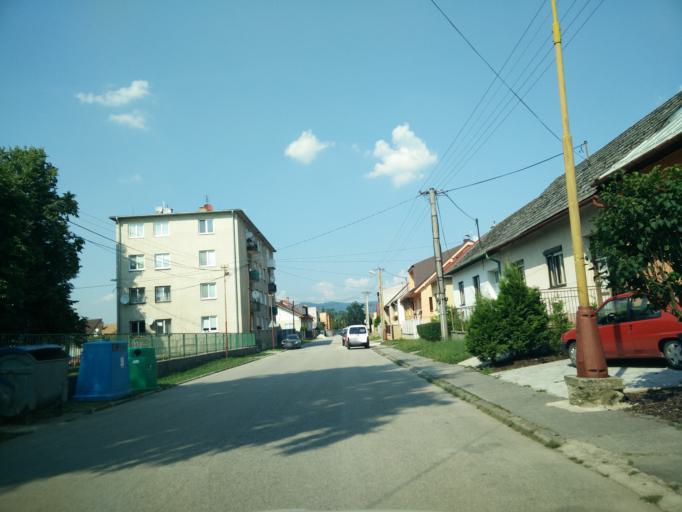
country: SK
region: Zilinsky
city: Rajec
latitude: 49.0856
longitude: 18.6416
